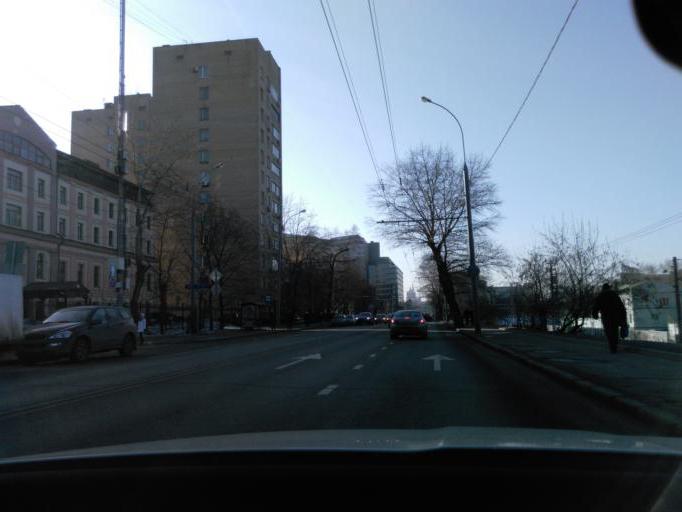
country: RU
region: Moscow
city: Mar'ina Roshcha
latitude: 55.7827
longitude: 37.5865
